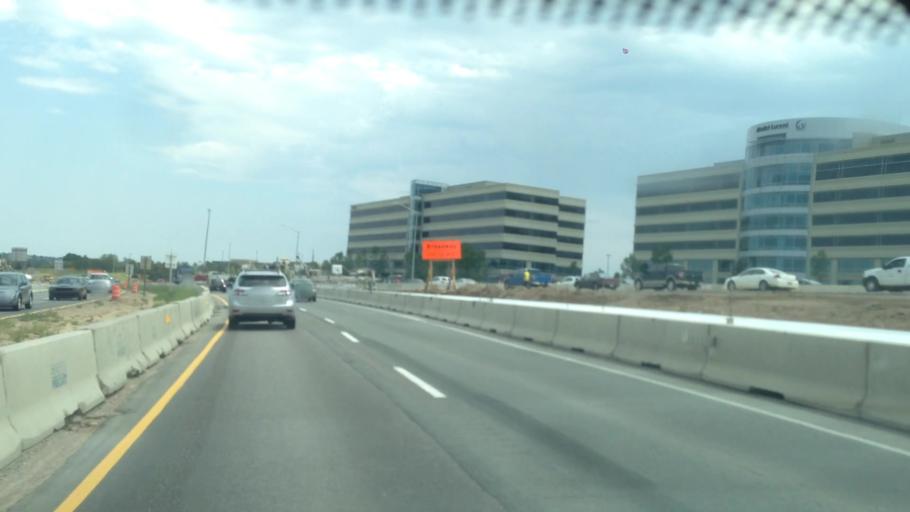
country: US
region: Colorado
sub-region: Douglas County
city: Highlands Ranch
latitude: 39.5591
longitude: -105.0052
